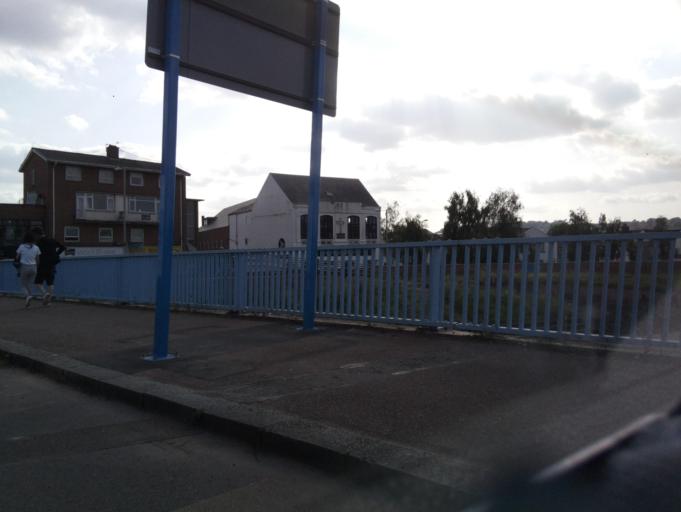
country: GB
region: England
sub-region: Devon
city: Exeter
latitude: 50.7186
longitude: -3.5383
